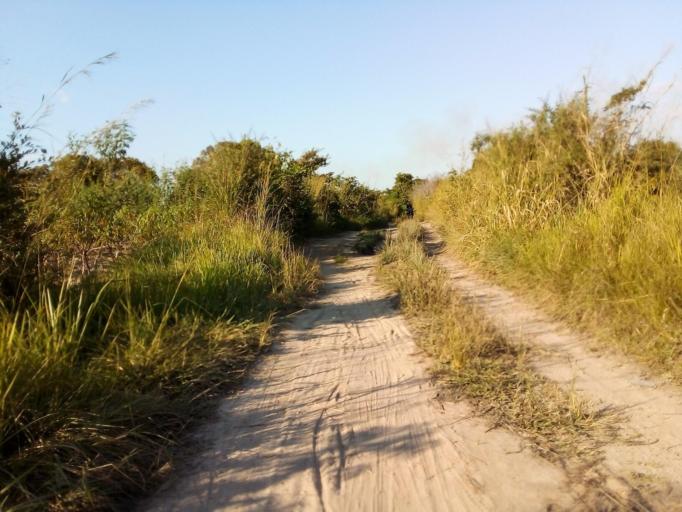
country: MZ
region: Zambezia
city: Quelimane
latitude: -17.5498
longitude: 36.7091
